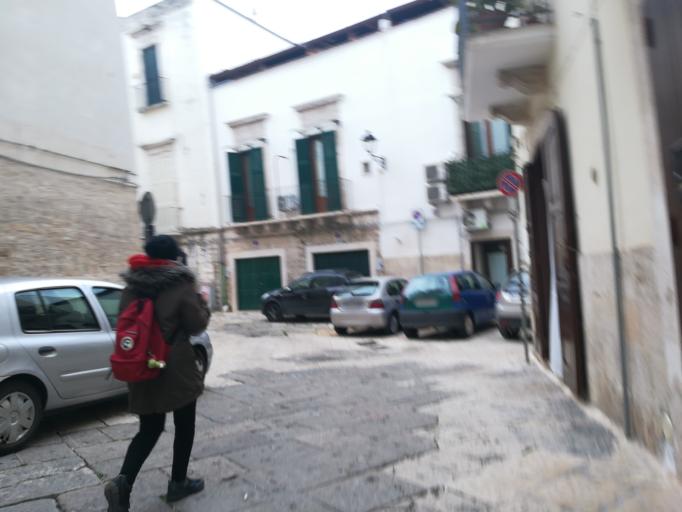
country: IT
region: Apulia
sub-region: Provincia di Bari
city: Bitonto
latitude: 41.1069
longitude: 16.6913
